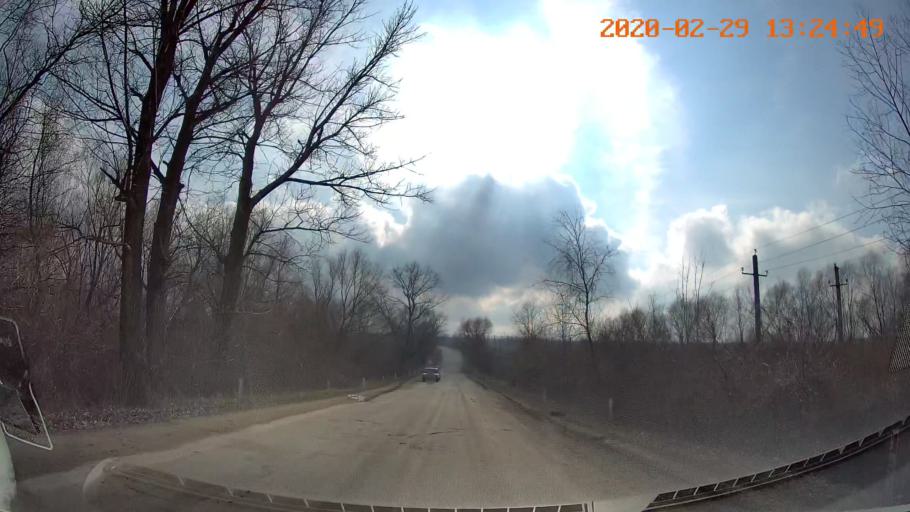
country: MD
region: Telenesti
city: Camenca
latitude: 47.9350
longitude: 28.6285
